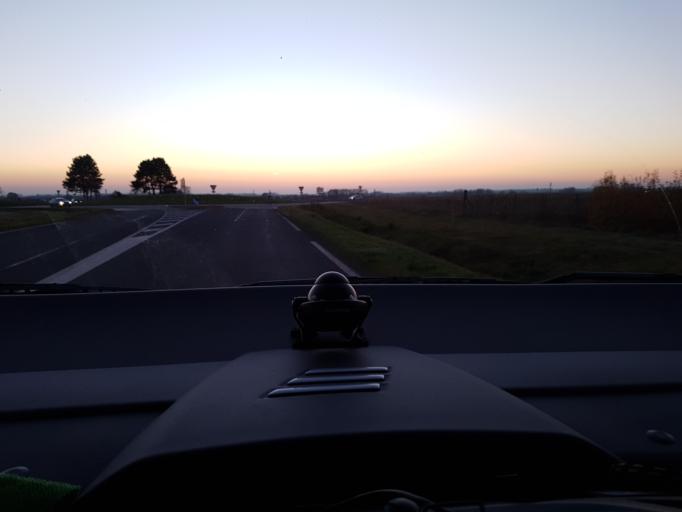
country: FR
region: Picardie
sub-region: Departement de la Somme
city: Rue
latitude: 50.2502
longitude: 1.7341
